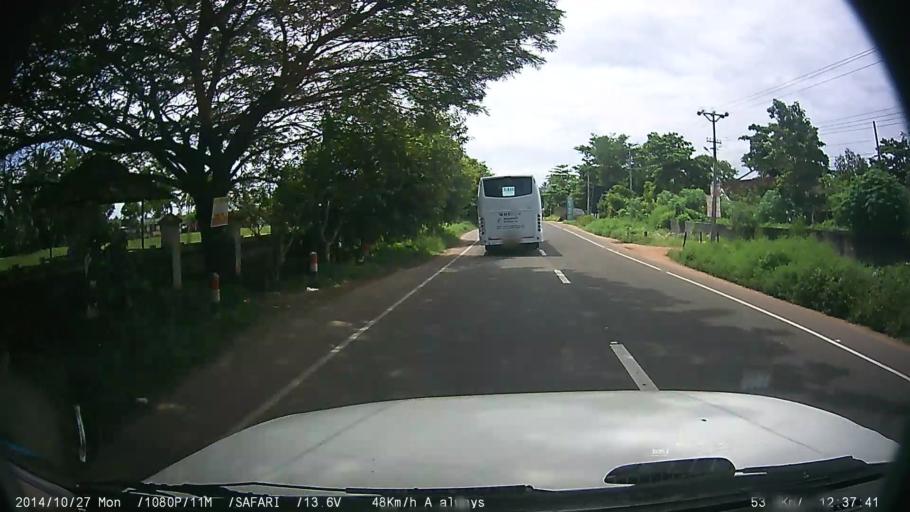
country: IN
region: Kerala
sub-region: Kottayam
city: Changanacheri
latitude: 9.4341
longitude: 76.5334
